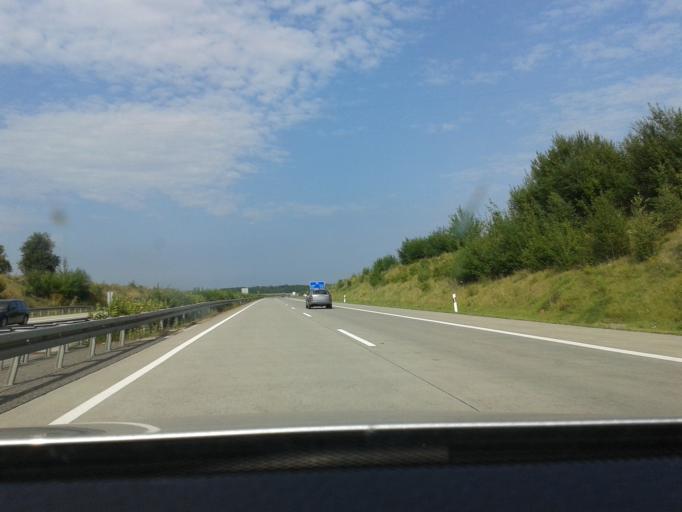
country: DE
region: Thuringia
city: Heilbad Heiligenstadt
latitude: 51.3998
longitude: 10.1347
